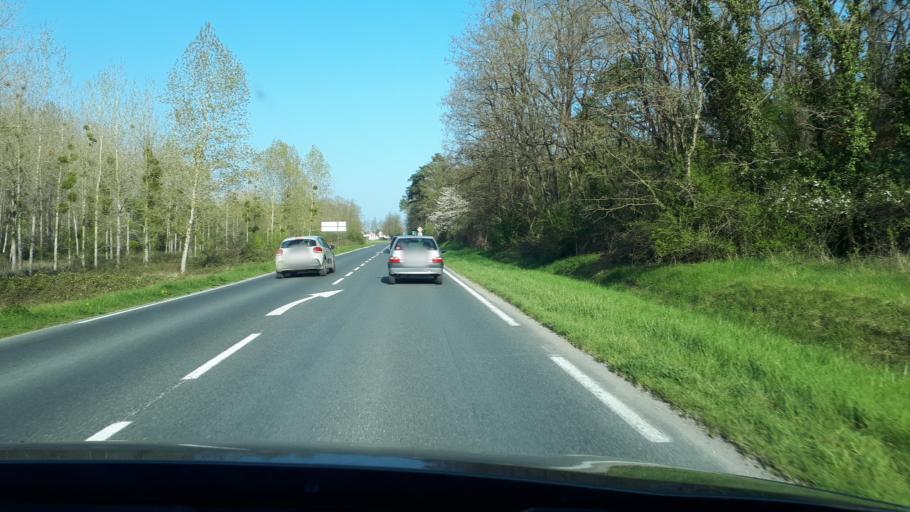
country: FR
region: Centre
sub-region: Departement du Loir-et-Cher
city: Saint-Georges-sur-Cher
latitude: 47.3224
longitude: 1.0939
